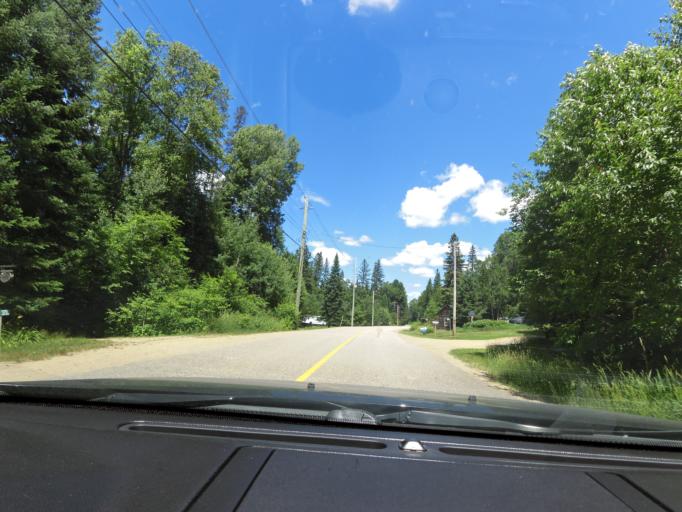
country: CA
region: Ontario
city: Huntsville
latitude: 45.6174
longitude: -79.1576
